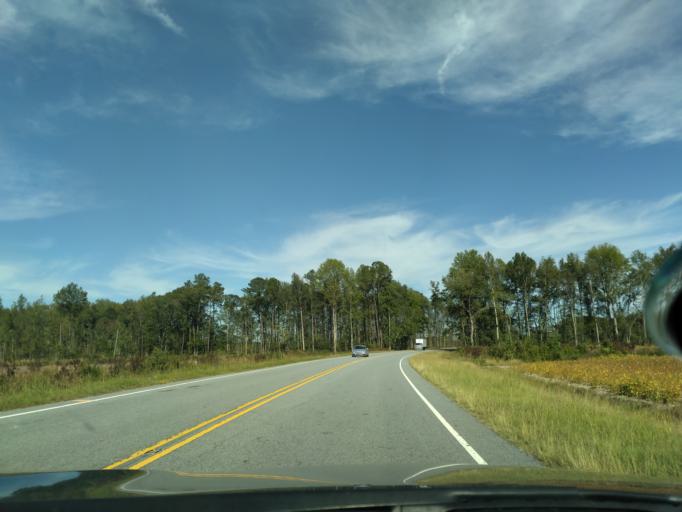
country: US
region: North Carolina
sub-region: Beaufort County
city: River Road
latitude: 35.5221
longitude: -76.8912
